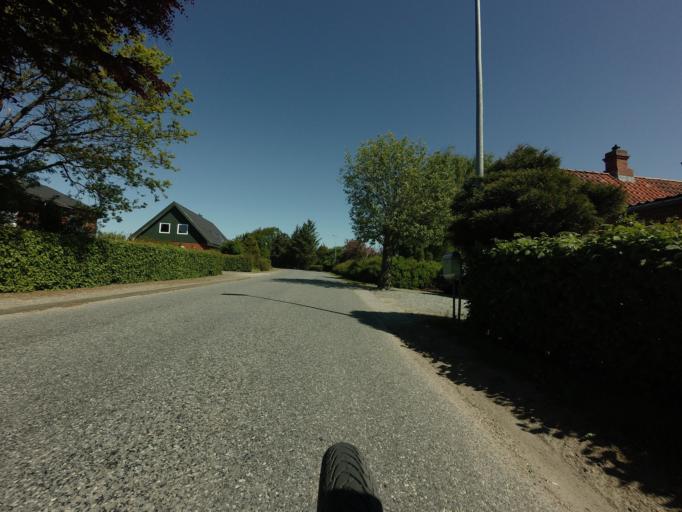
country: DK
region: North Denmark
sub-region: Hjorring Kommune
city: Hjorring
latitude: 57.4342
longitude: 9.9029
